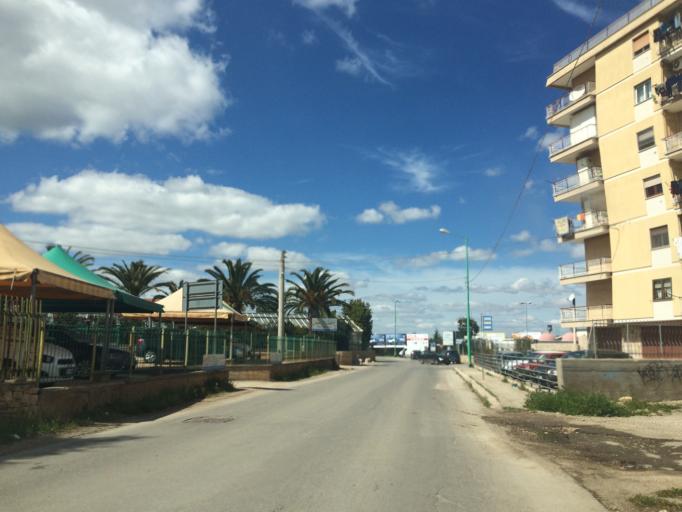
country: IT
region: Apulia
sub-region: Provincia di Bari
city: Terlizzi
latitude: 41.1281
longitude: 16.5355
